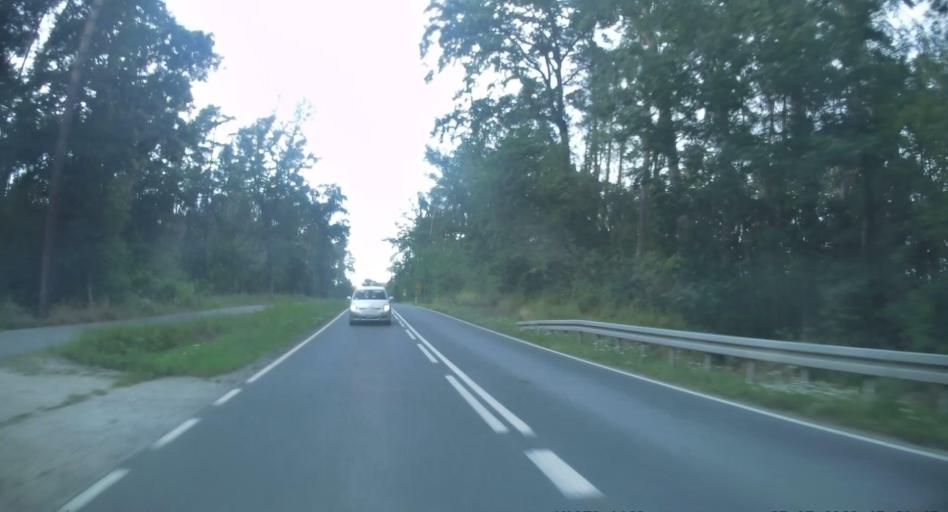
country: PL
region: Lesser Poland Voivodeship
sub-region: Powiat brzeski
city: Przyborow
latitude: 50.0555
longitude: 20.6393
